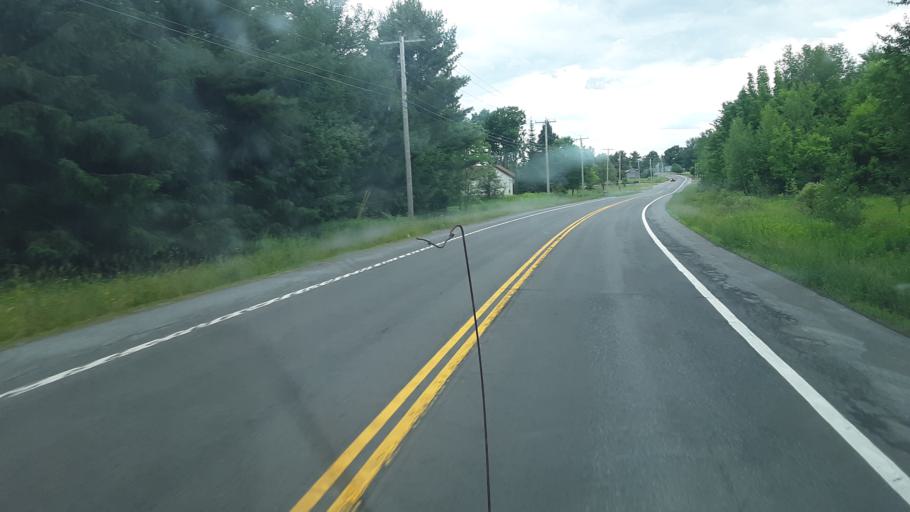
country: US
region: New York
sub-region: Oneida County
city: Rome
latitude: 43.3382
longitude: -75.4762
